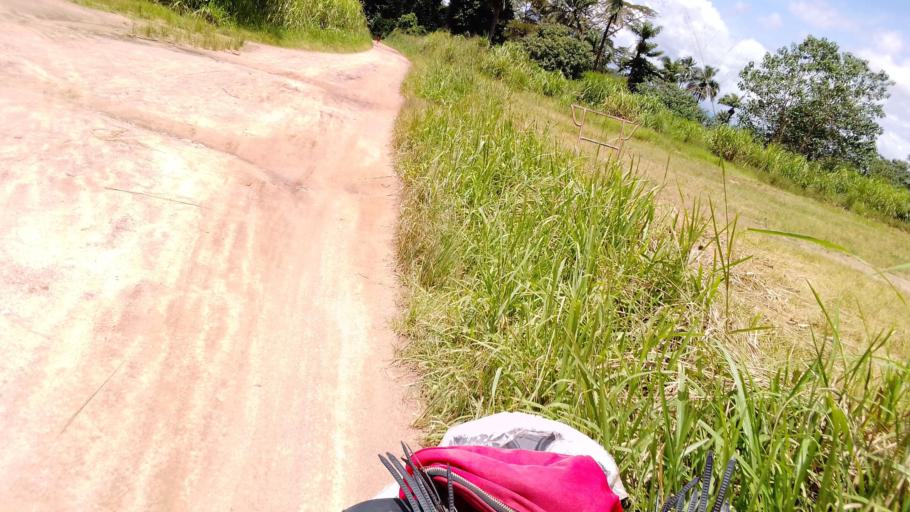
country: SL
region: Eastern Province
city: Koidu
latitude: 8.6954
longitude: -10.9537
